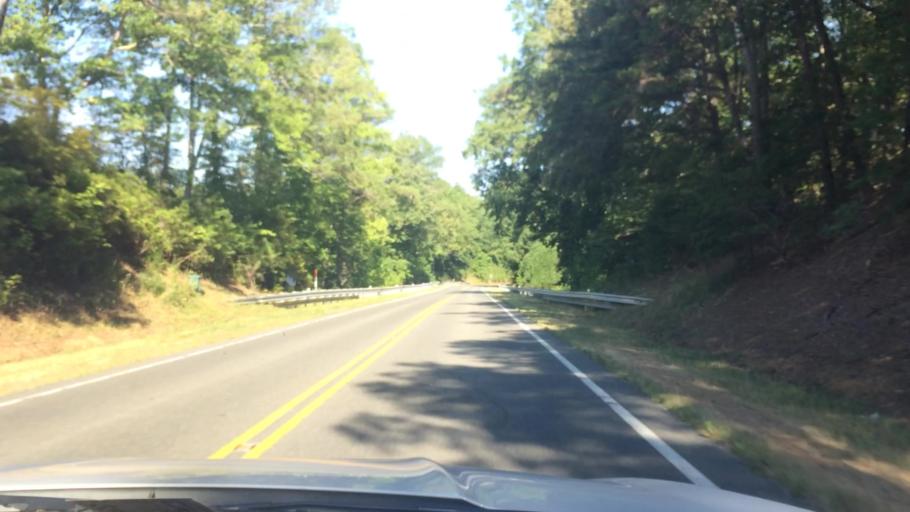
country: US
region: Virginia
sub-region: Lancaster County
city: Lancaster
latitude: 37.8279
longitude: -76.5712
